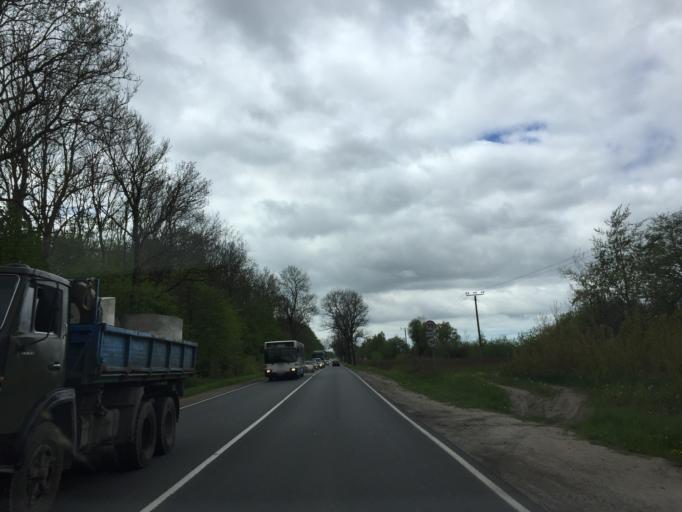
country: RU
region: Kaliningrad
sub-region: Gorod Kaliningrad
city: Kaliningrad
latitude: 54.6554
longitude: 20.3853
